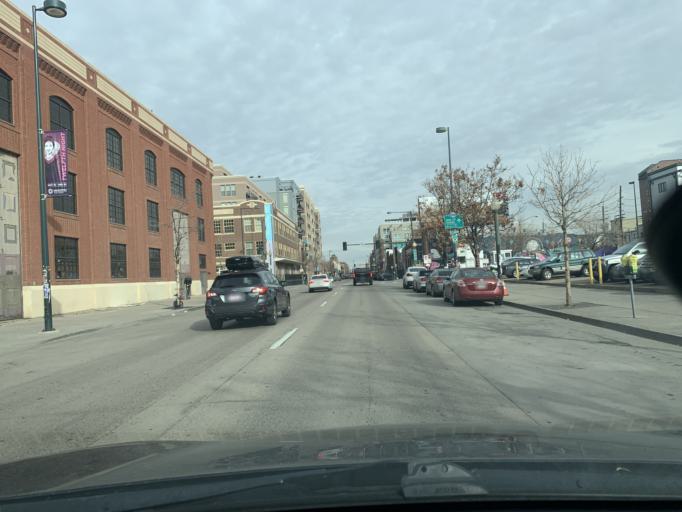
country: US
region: Colorado
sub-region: Denver County
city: Denver
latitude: 39.7541
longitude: -104.9928
